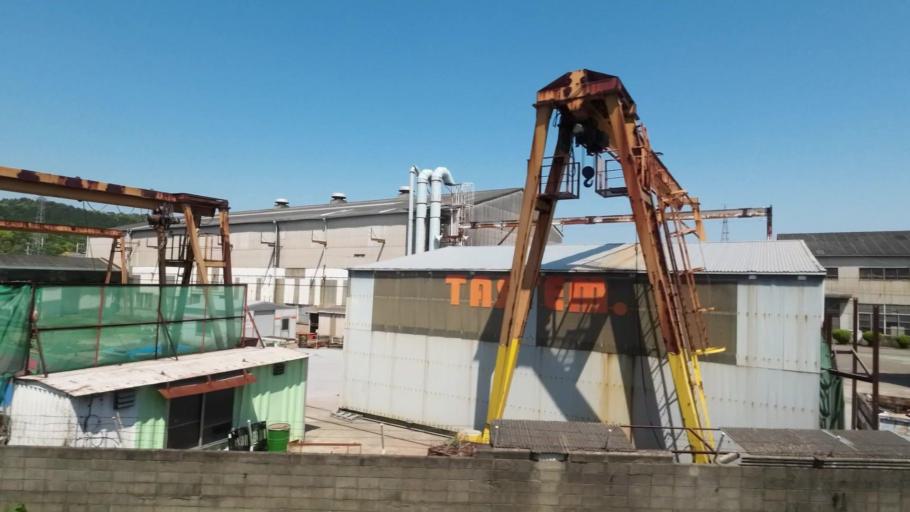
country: JP
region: Ehime
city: Niihama
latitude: 33.9416
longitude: 133.2875
